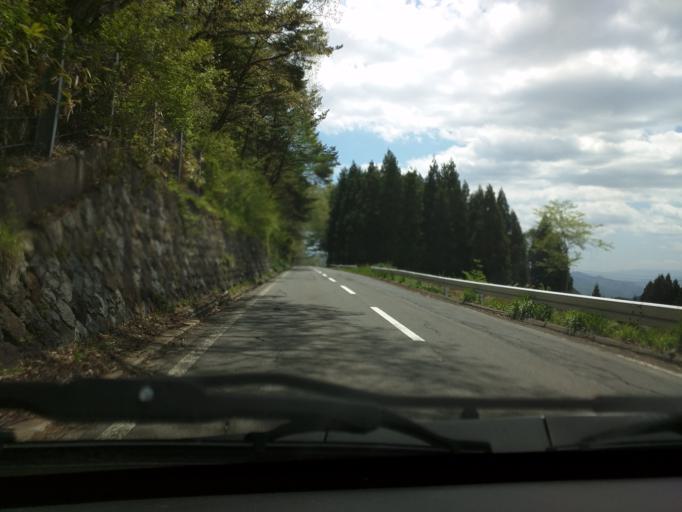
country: JP
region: Nagano
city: Nagano-shi
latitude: 36.6870
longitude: 138.1590
